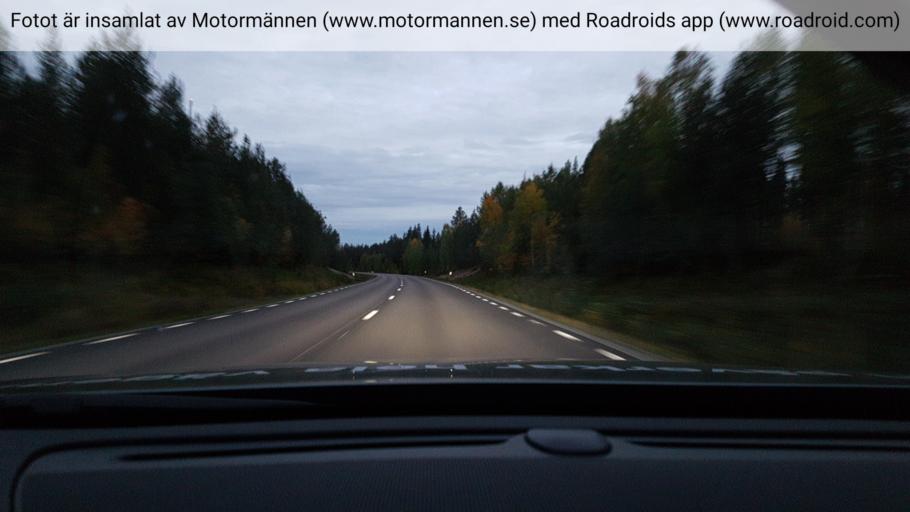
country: SE
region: Norrbotten
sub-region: Alvsbyns Kommun
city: AElvsbyn
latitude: 65.7186
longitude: 20.9866
